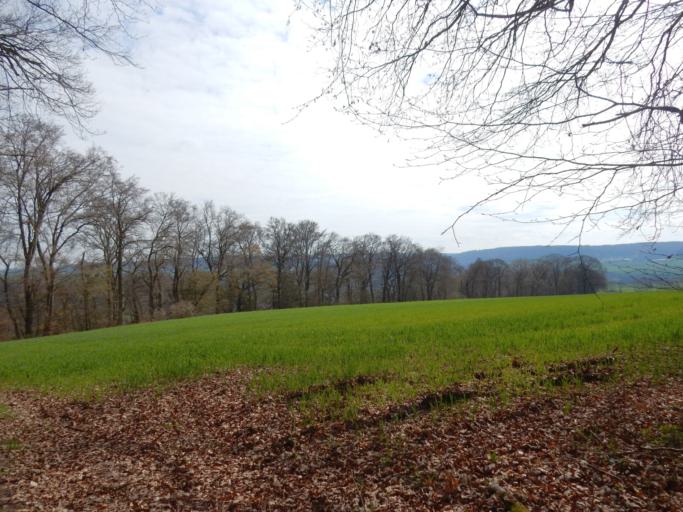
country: LU
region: Diekirch
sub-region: Canton de Diekirch
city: Reisdorf
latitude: 49.8828
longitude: 6.2497
